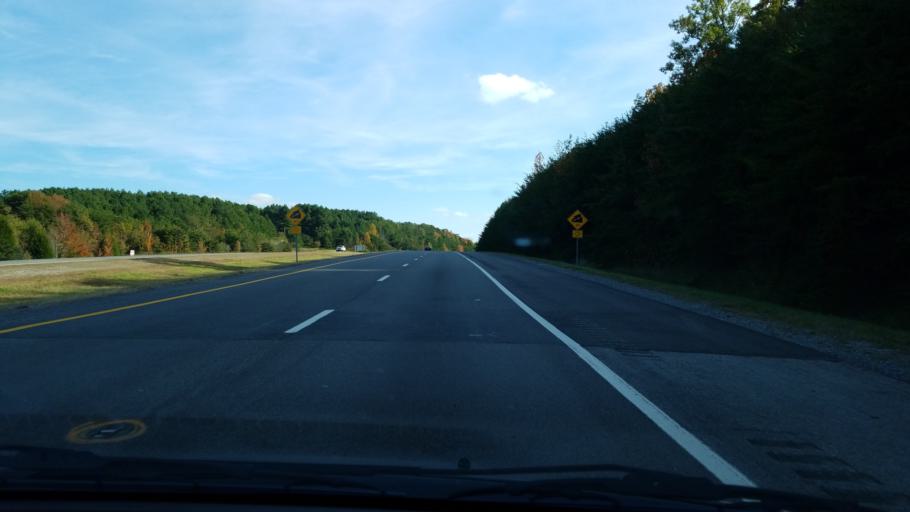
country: US
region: Tennessee
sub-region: Hamilton County
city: Sale Creek
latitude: 35.3420
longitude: -85.1697
